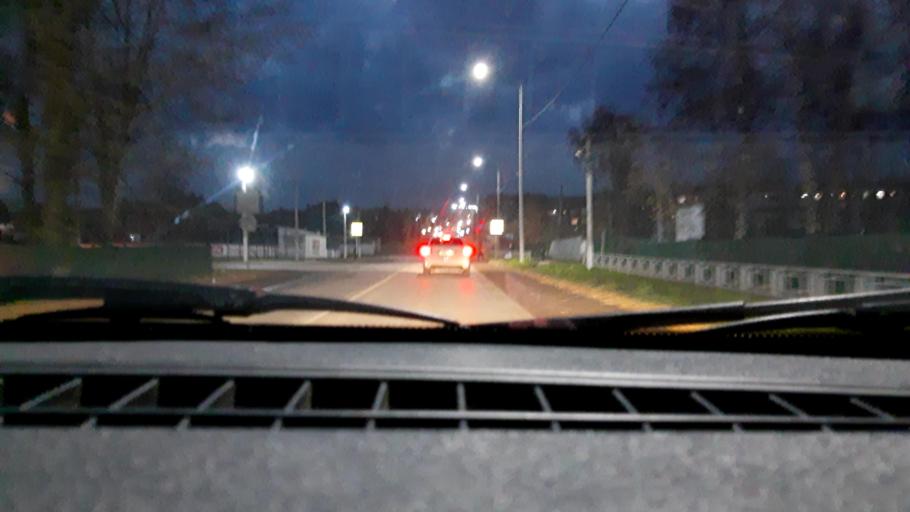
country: RU
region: Bashkortostan
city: Mikhaylovka
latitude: 54.8053
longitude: 55.8909
